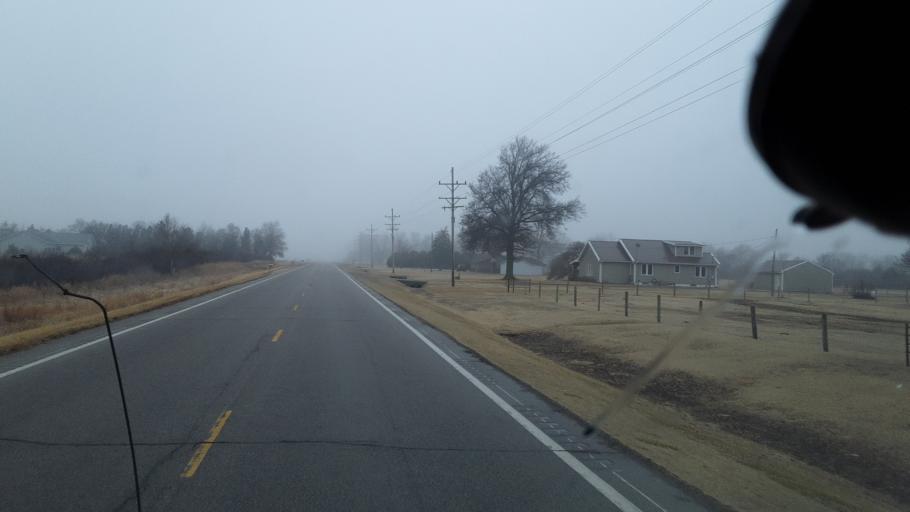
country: US
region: Kansas
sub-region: Reno County
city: South Hutchinson
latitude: 37.9657
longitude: -97.9403
